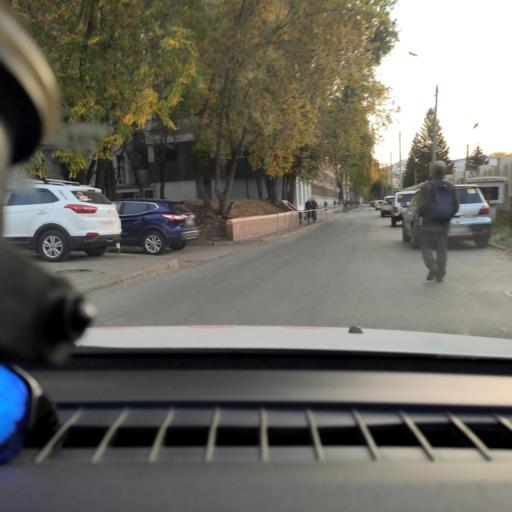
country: RU
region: Samara
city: Samara
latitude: 53.2018
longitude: 50.1061
